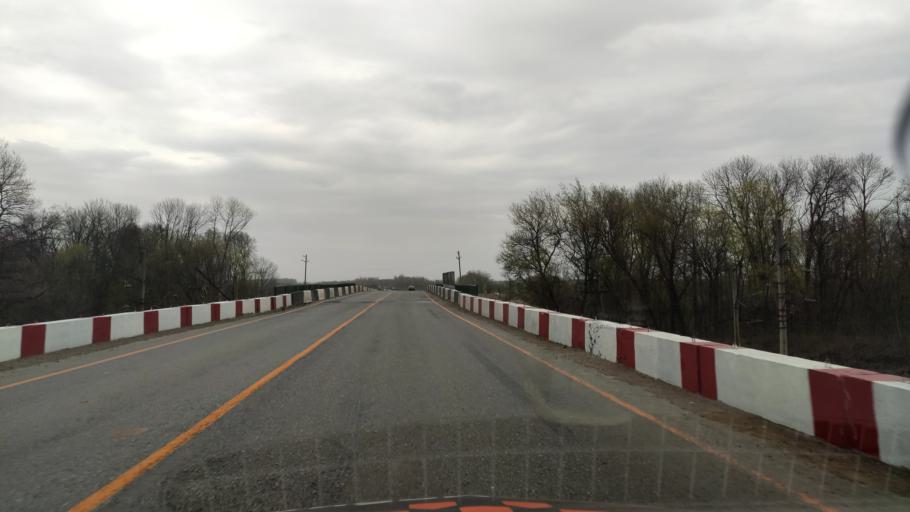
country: RU
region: Kursk
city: Gorshechnoye
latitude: 51.5520
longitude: 38.0379
